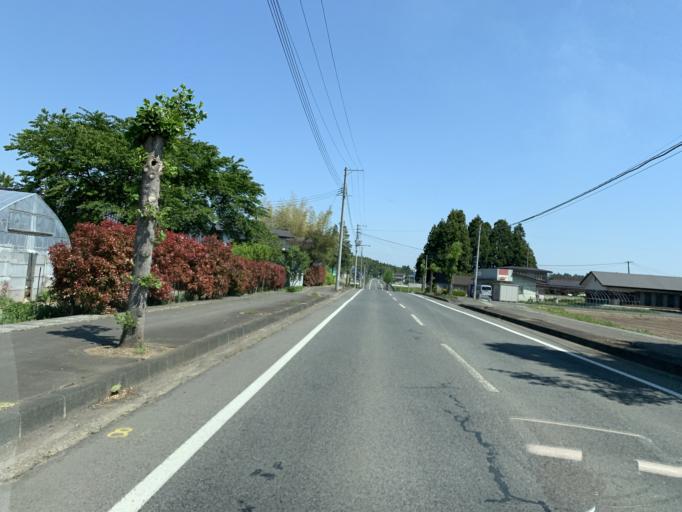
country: JP
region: Iwate
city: Mizusawa
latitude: 39.2028
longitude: 141.0950
